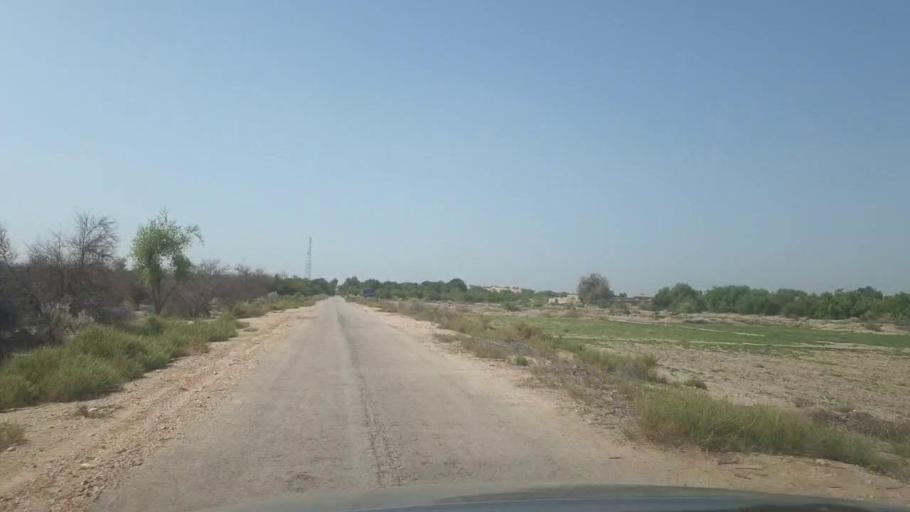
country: PK
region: Sindh
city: Rohri
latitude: 27.4116
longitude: 69.0804
